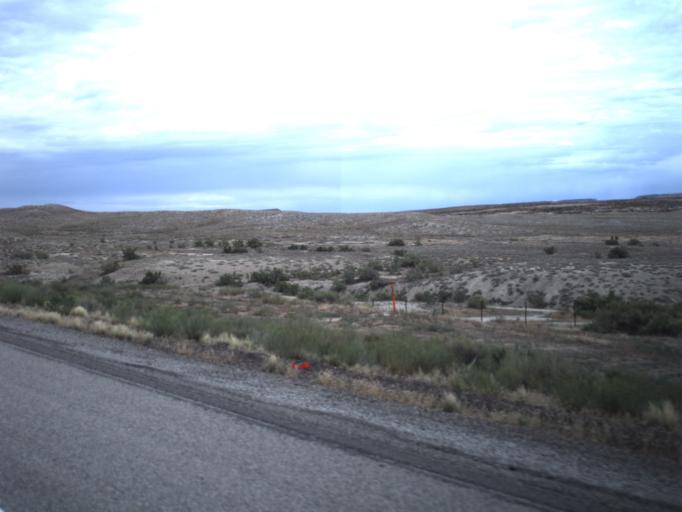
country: US
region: Utah
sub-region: Grand County
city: Moab
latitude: 39.0153
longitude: -109.3031
